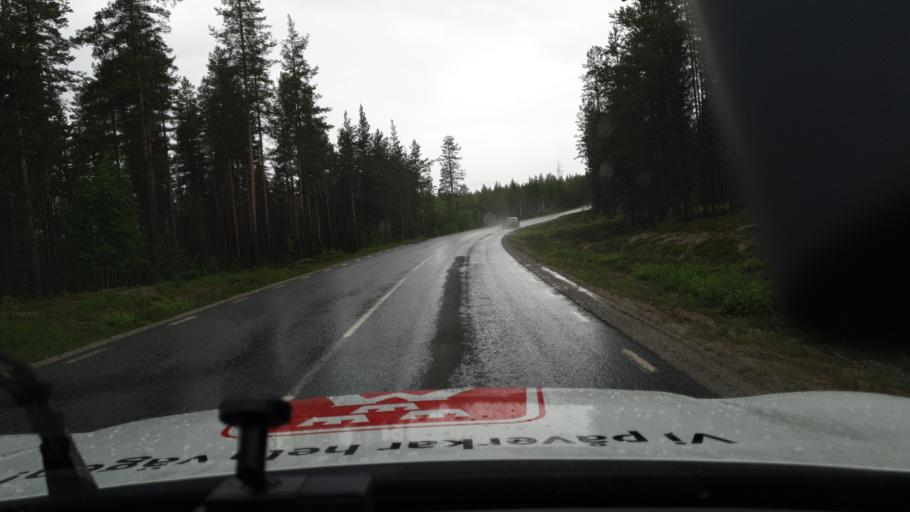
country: SE
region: Vaesterbotten
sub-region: Lycksele Kommun
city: Lycksele
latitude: 64.4868
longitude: 18.8974
